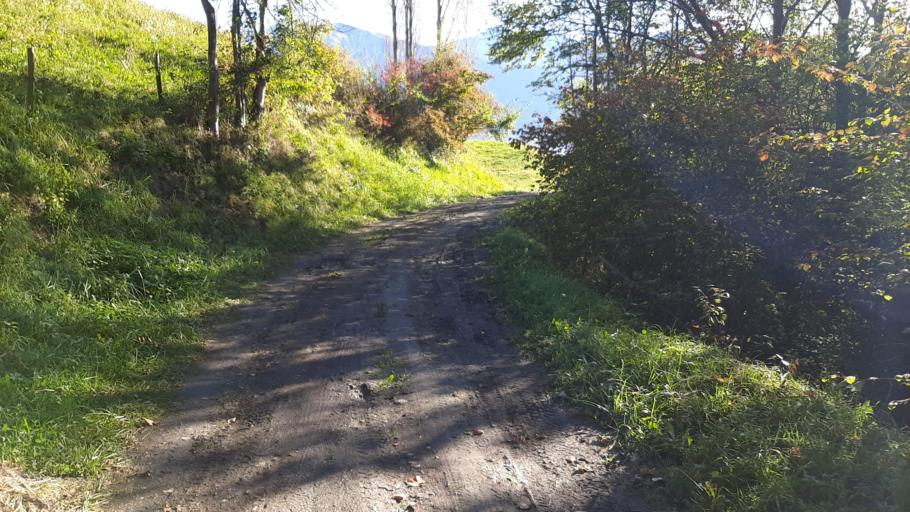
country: FR
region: Rhone-Alpes
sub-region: Departement de la Savoie
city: Saint-Jean-de-Maurienne
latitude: 45.2735
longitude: 6.3119
